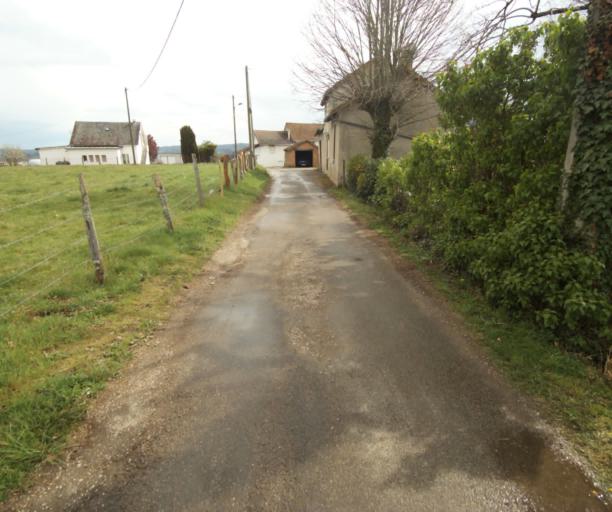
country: FR
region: Limousin
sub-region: Departement de la Correze
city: Tulle
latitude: 45.2661
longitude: 1.7546
